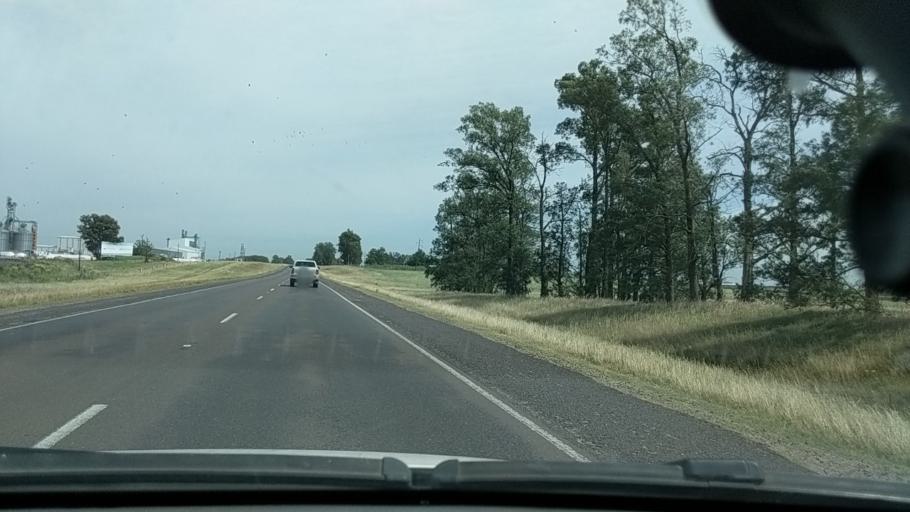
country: UY
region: Durazno
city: Durazno
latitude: -33.4987
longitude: -56.4250
